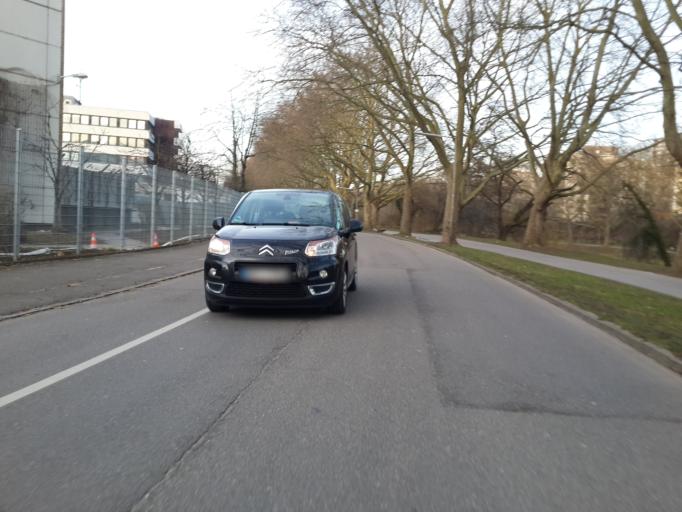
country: DE
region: Baden-Wuerttemberg
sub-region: Regierungsbezirk Stuttgart
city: Heilbronn
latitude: 49.1345
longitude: 9.2075
